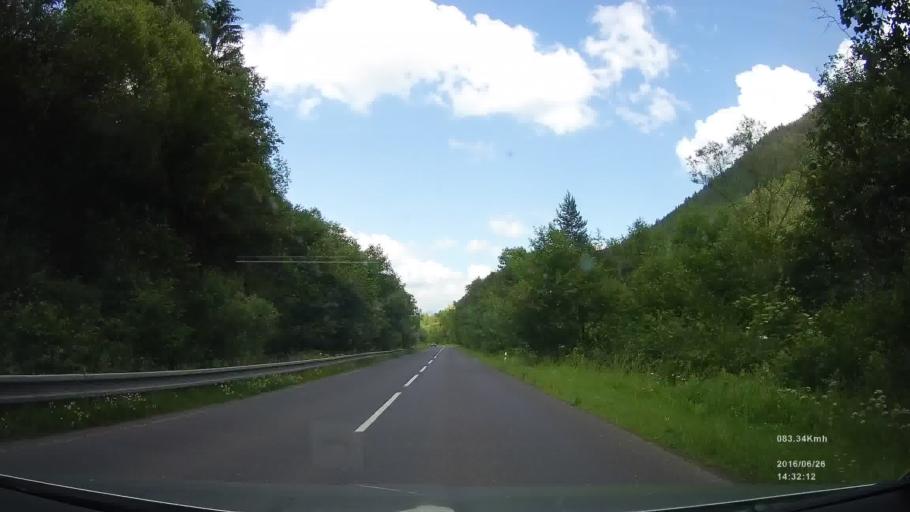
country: SK
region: Zilinsky
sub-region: Okres Zilina
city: Liptovsky Hradok
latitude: 49.0099
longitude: 19.7683
